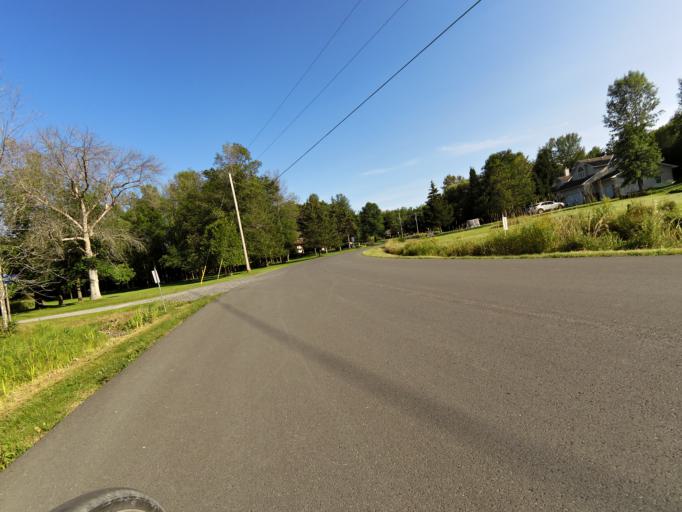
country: CA
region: Ontario
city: Bells Corners
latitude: 45.4774
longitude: -76.0324
